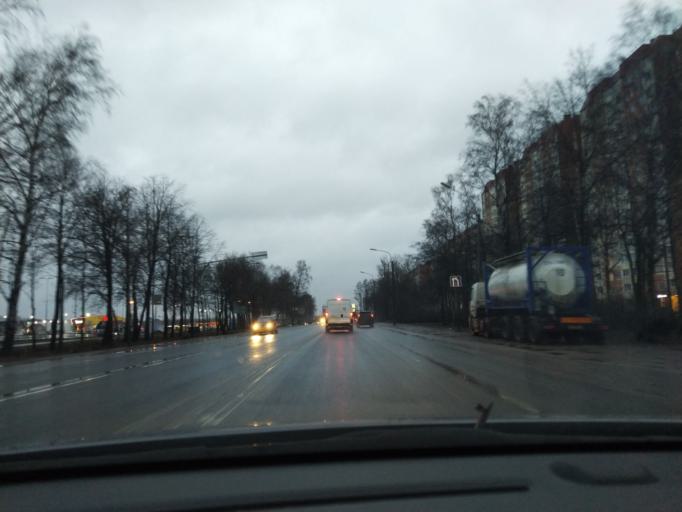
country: RU
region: St.-Petersburg
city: Gorelovo
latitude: 59.7915
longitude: 30.1468
